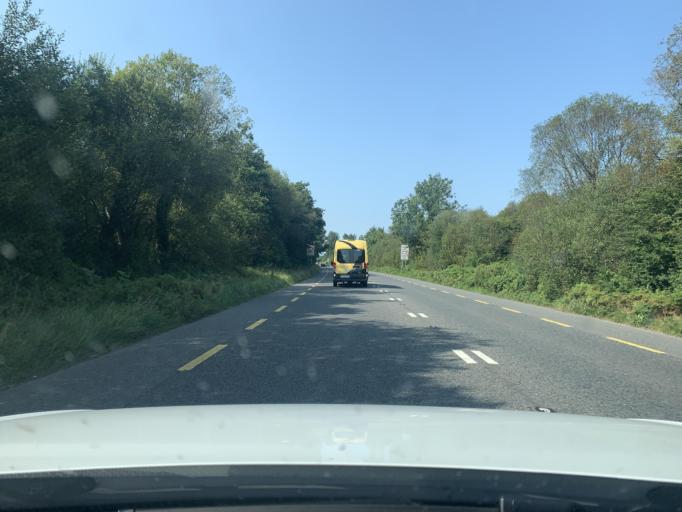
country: IE
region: Leinster
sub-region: An Iarmhi
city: Athlone
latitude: 53.4516
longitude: -7.9886
